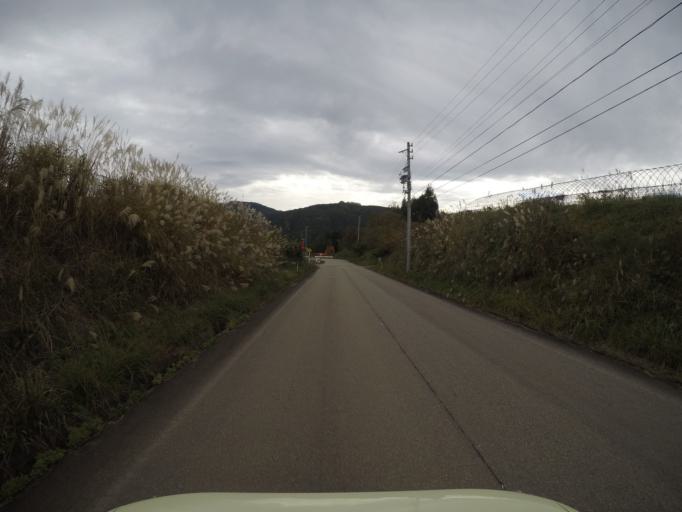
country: JP
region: Gifu
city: Takayama
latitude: 36.1446
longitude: 137.3393
